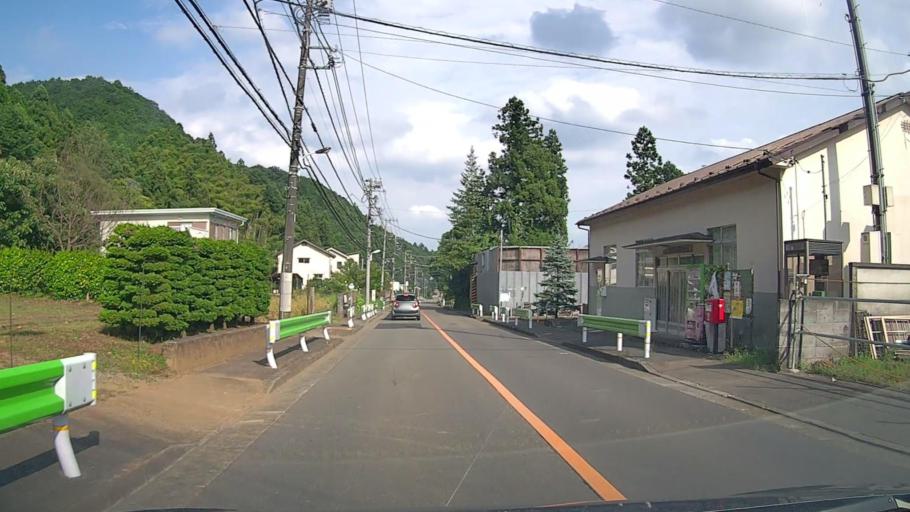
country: JP
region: Tokyo
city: Itsukaichi
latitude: 35.7112
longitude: 139.2360
